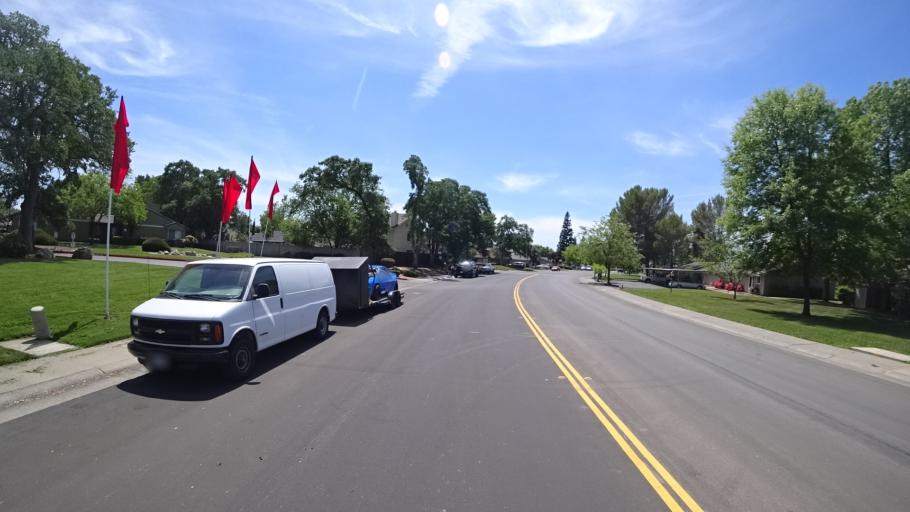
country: US
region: California
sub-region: Placer County
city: Rocklin
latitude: 38.7805
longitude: -121.2384
